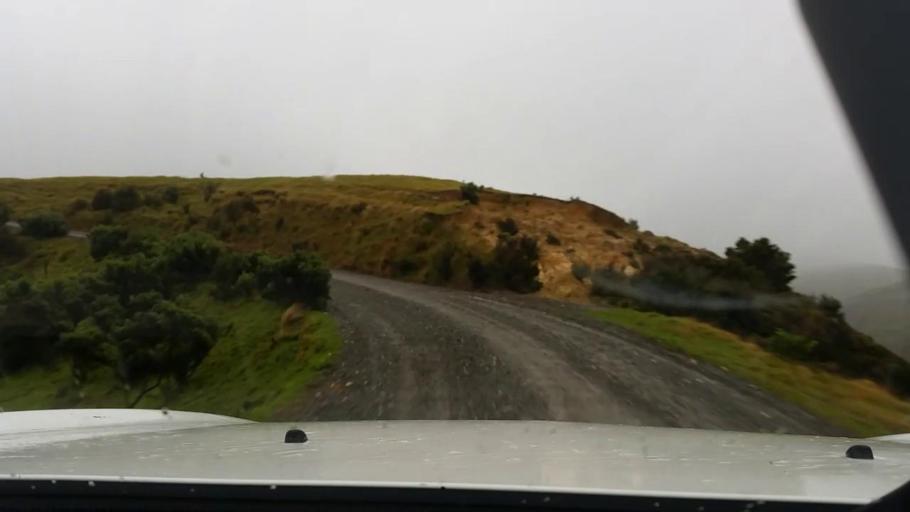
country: NZ
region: Wellington
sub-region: Masterton District
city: Masterton
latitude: -41.2501
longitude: 175.8959
